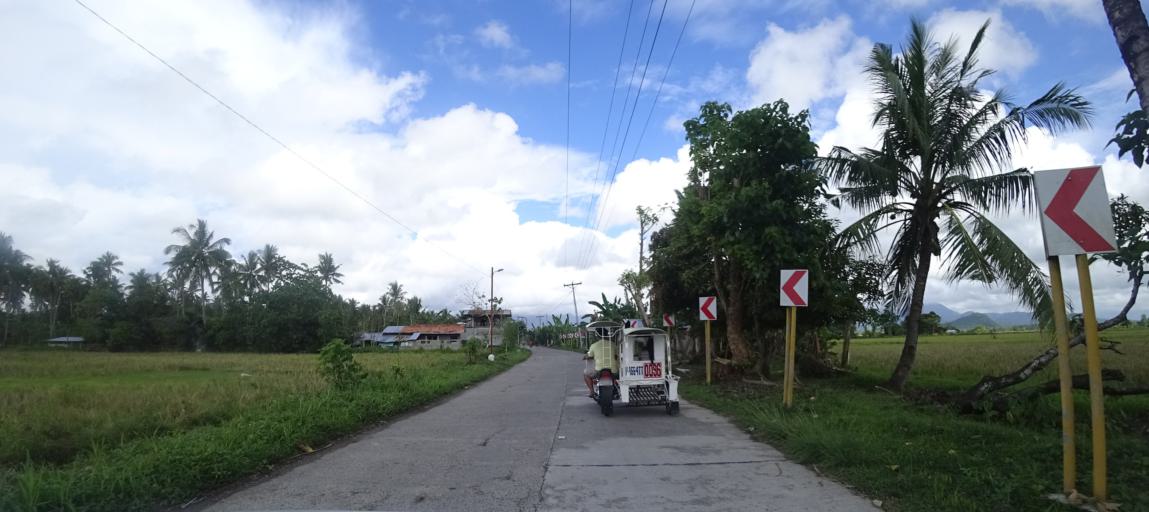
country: PH
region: Eastern Visayas
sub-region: Province of Leyte
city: MacArthur
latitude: 10.8196
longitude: 124.9851
